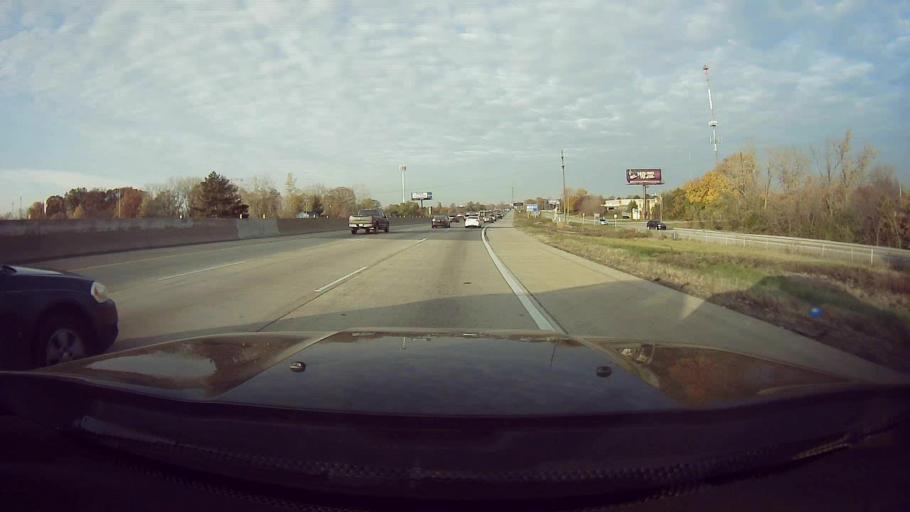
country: US
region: Michigan
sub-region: Macomb County
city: Saint Clair Shores
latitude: 42.5399
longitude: -82.8883
